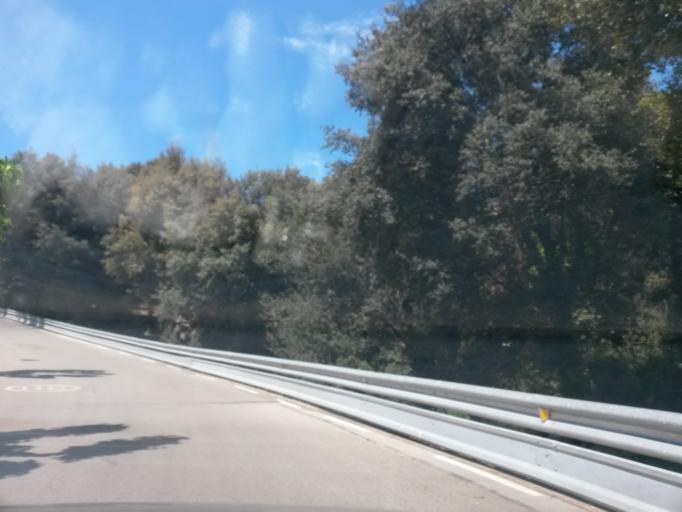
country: ES
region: Catalonia
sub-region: Provincia de Girona
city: Vilablareix
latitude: 41.9635
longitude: 2.7619
